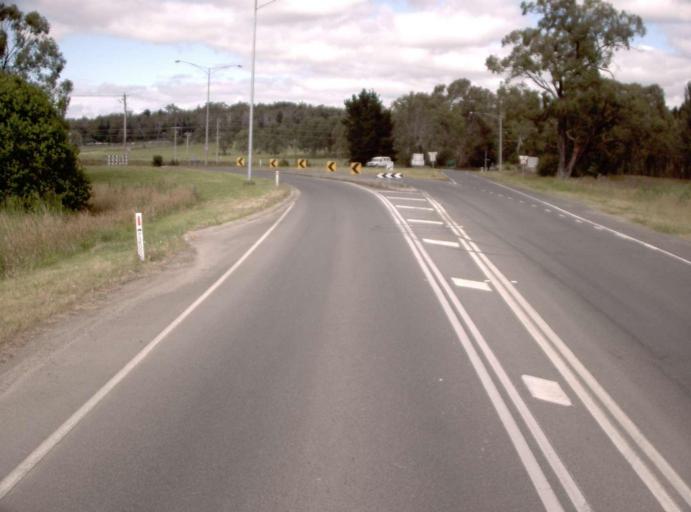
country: AU
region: Victoria
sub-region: Latrobe
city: Morwell
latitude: -38.1996
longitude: 146.4396
